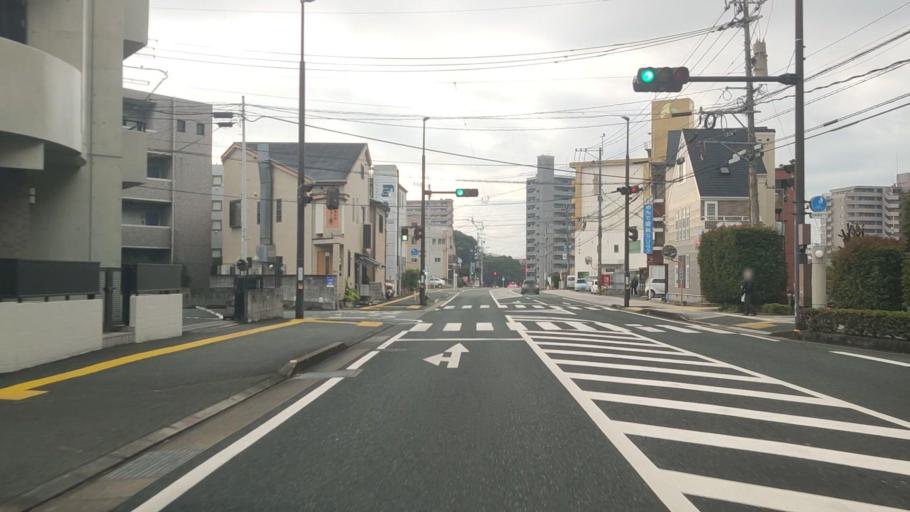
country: JP
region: Kumamoto
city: Kumamoto
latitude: 32.7896
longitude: 130.7392
